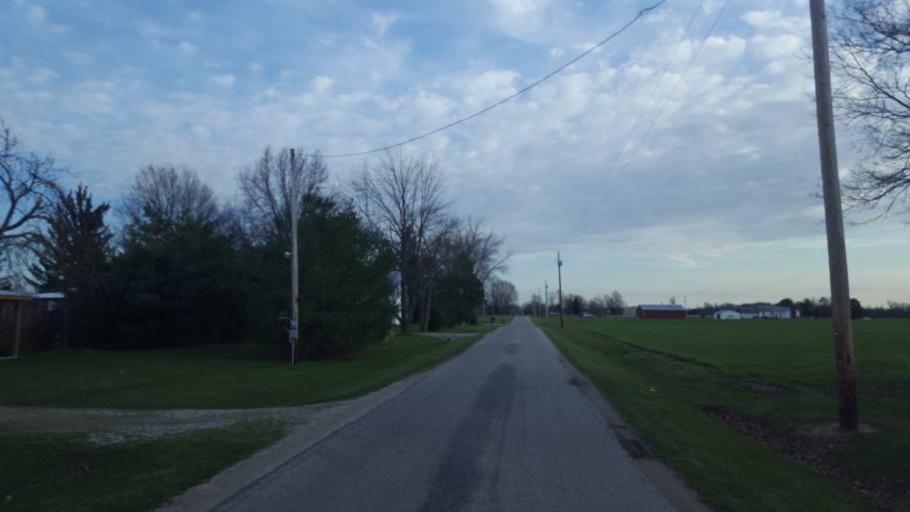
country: US
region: Ohio
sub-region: Crawford County
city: Bucyrus
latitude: 40.6775
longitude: -82.9484
